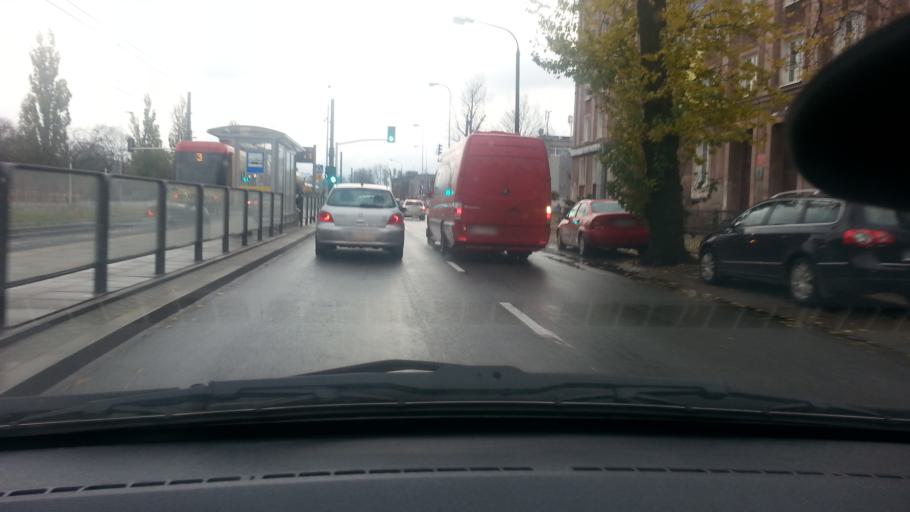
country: PL
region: Masovian Voivodeship
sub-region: Warszawa
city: Targowek
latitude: 52.2789
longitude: 21.0271
